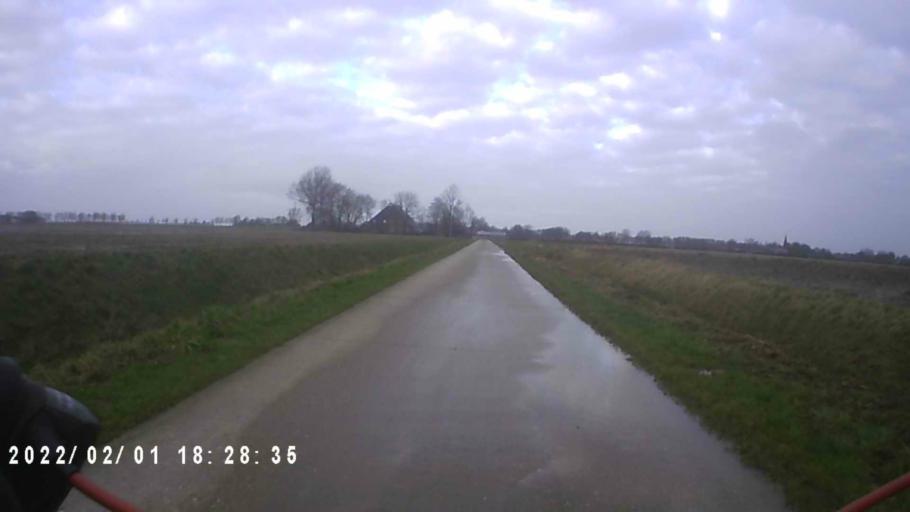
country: NL
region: Groningen
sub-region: Gemeente De Marne
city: Ulrum
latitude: 53.3522
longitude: 6.3194
